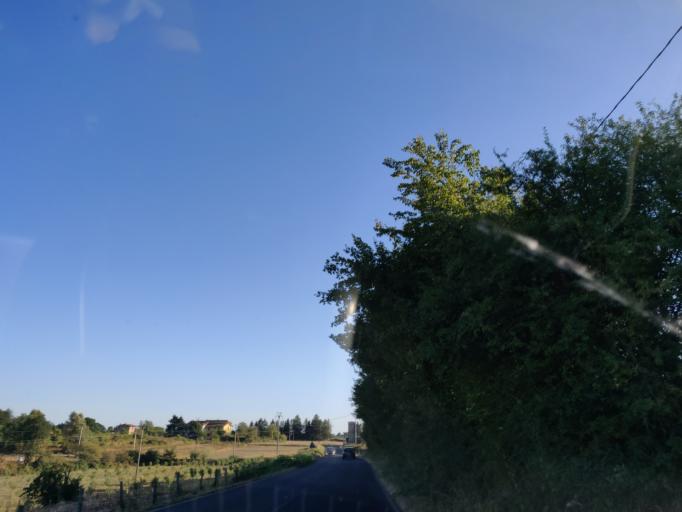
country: IT
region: Latium
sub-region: Provincia di Viterbo
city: Acquapendente
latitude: 42.7345
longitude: 11.8770
